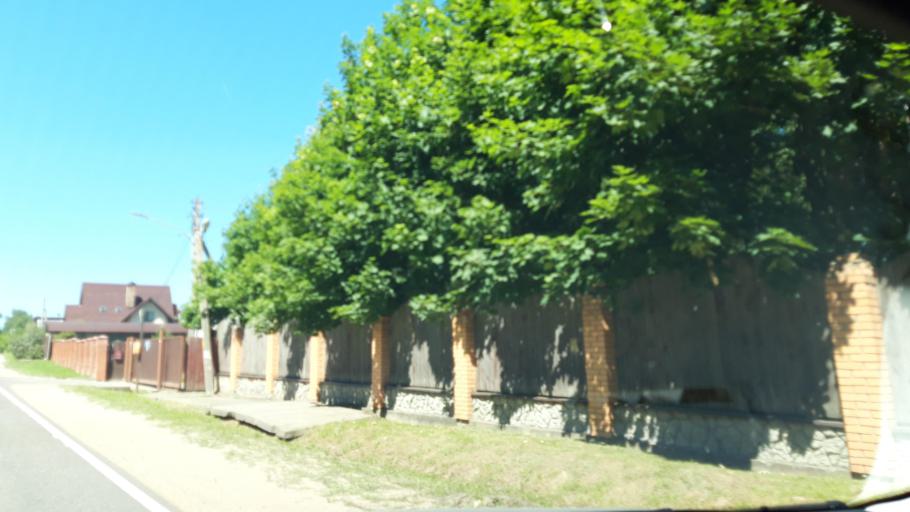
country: RU
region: Moskovskaya
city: Solnechnogorsk
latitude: 56.1655
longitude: 36.9709
